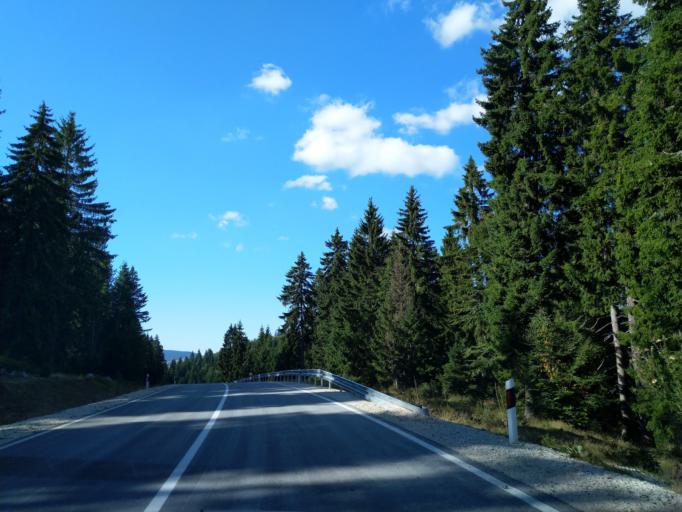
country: RS
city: Sokolovica
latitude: 43.2951
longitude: 20.3087
